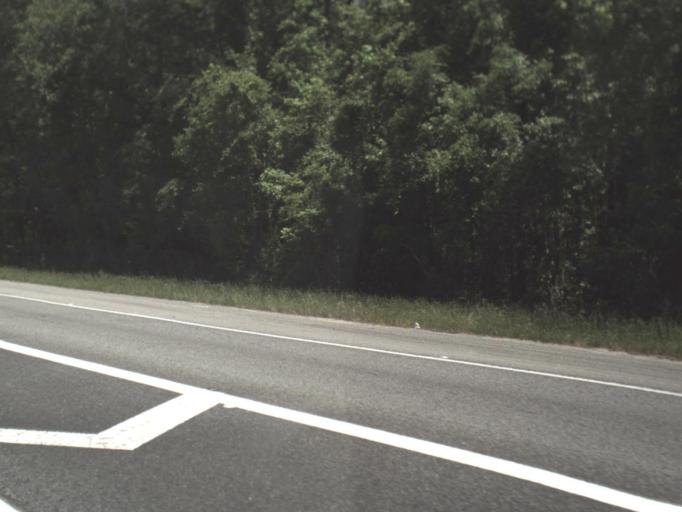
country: US
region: Florida
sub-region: Jefferson County
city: Monticello
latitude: 30.4887
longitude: -84.0206
